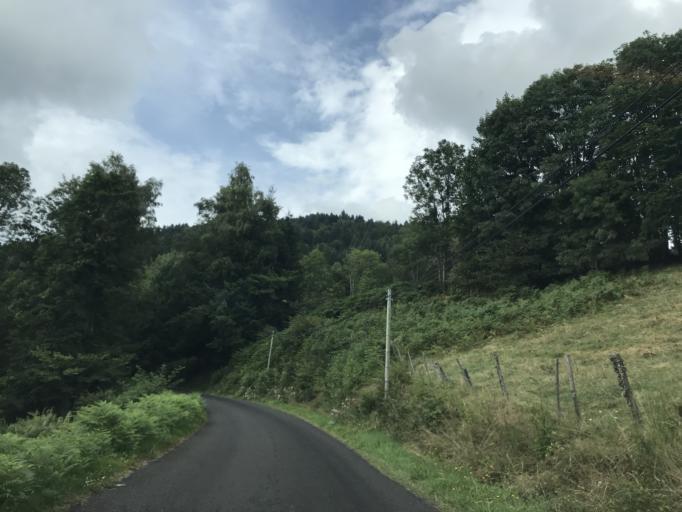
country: FR
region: Auvergne
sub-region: Departement du Puy-de-Dome
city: Job
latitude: 45.6702
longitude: 3.7565
